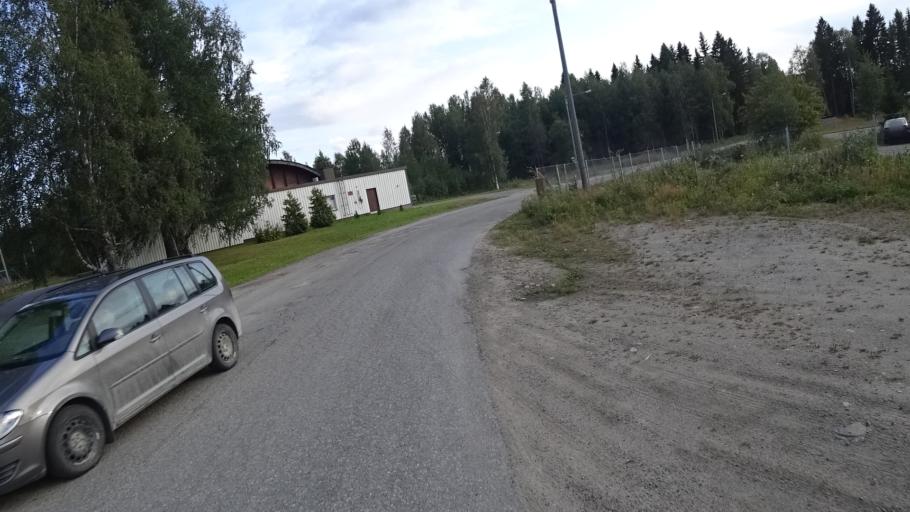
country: FI
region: North Karelia
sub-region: Joensuu
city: Ilomantsi
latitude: 62.6713
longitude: 30.9476
